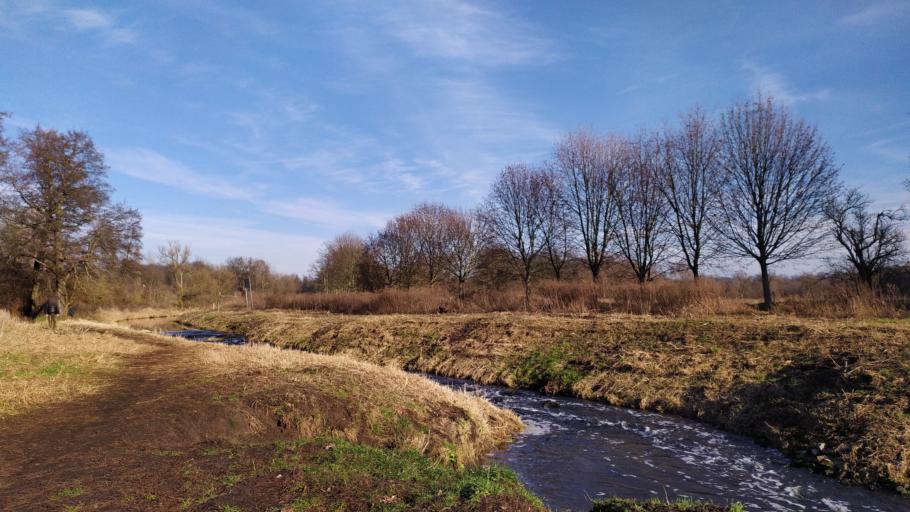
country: DE
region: Berlin
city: Friedrichshagen
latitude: 52.4774
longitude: 13.6342
